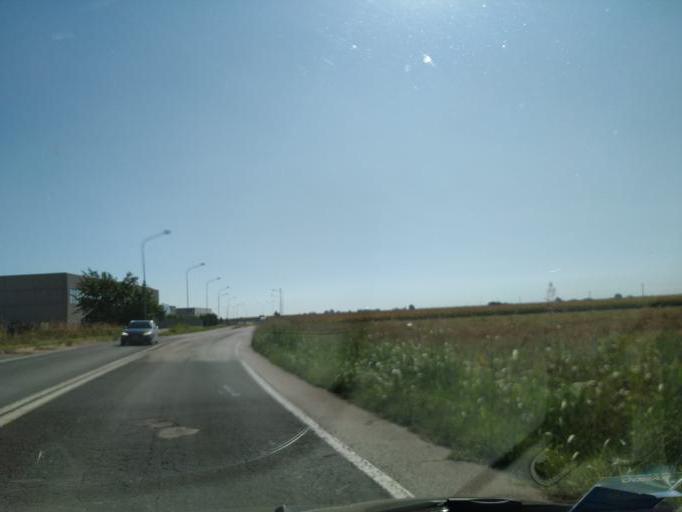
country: IT
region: Emilia-Romagna
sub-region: Provincia di Bologna
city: Decima
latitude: 44.6987
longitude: 11.2284
